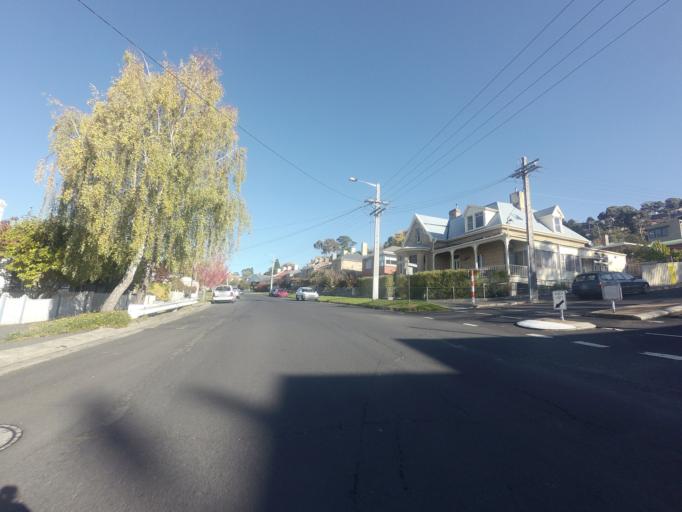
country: AU
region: Tasmania
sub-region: Hobart
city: Sandy Bay
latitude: -42.8820
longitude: 147.3097
